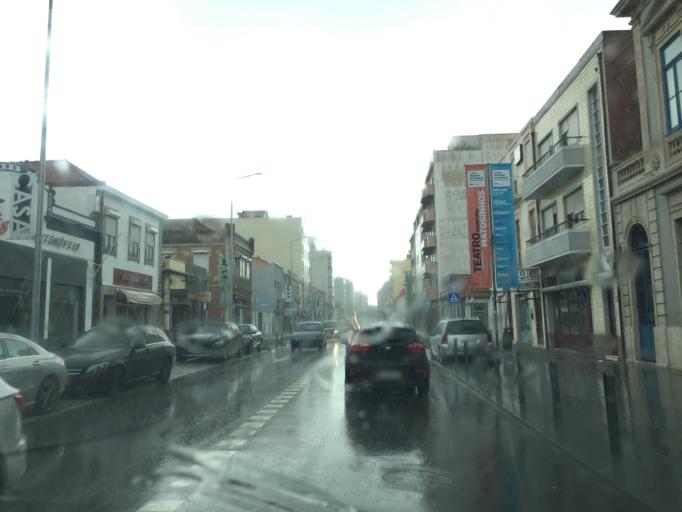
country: PT
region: Porto
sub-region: Matosinhos
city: Matosinhos
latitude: 41.1844
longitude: -8.6947
